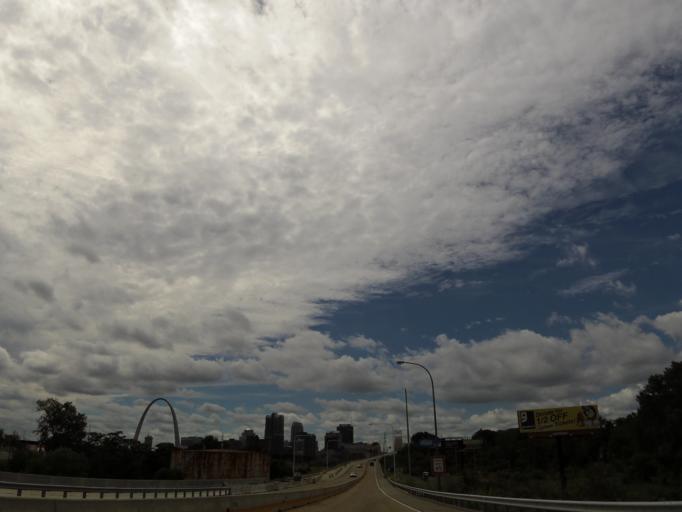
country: US
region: Illinois
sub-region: Saint Clair County
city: East Saint Louis
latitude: 38.6300
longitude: -90.1667
